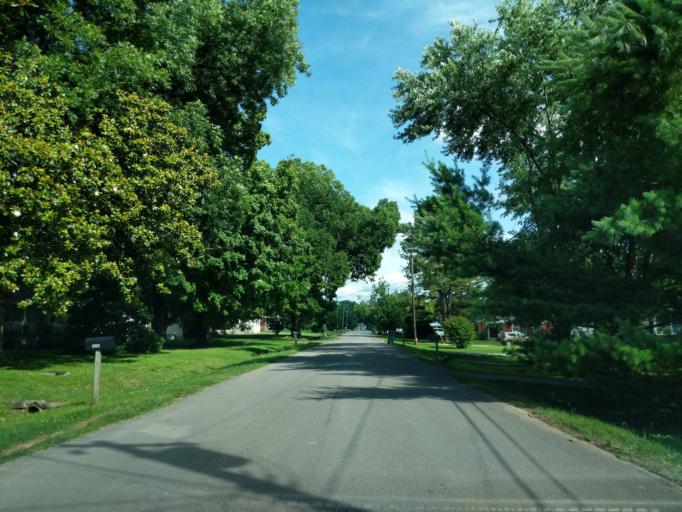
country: US
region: Tennessee
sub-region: Davidson County
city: Lakewood
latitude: 36.2744
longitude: -86.6698
